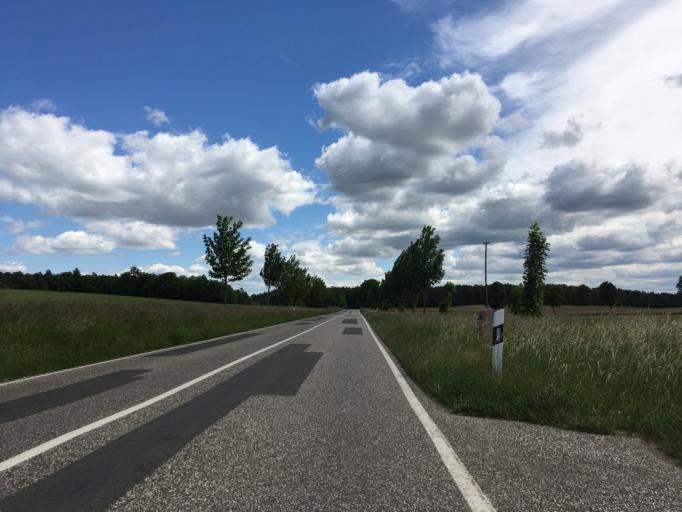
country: DE
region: Brandenburg
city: Protzel
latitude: 52.7096
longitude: 14.0106
